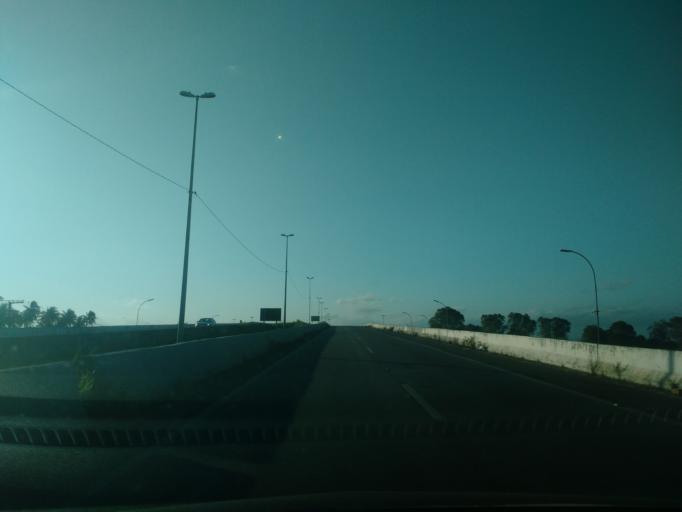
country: BR
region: Alagoas
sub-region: Satuba
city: Satuba
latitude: -9.5151
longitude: -35.8044
